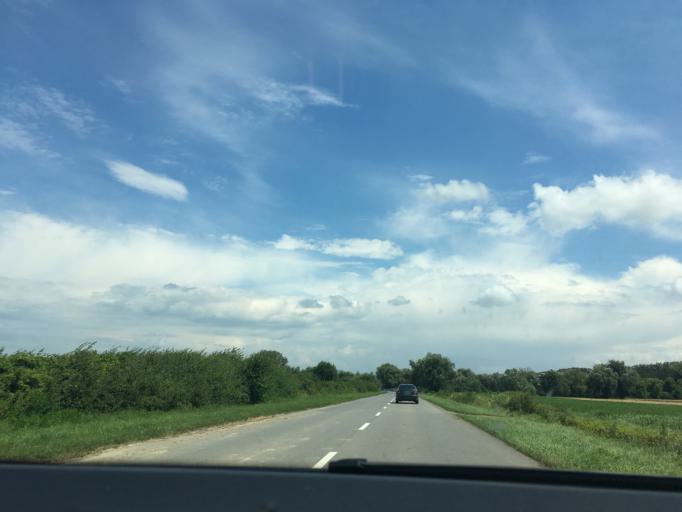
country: SK
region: Presovsky
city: Vranov nad Topl'ou
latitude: 48.8232
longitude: 21.7056
